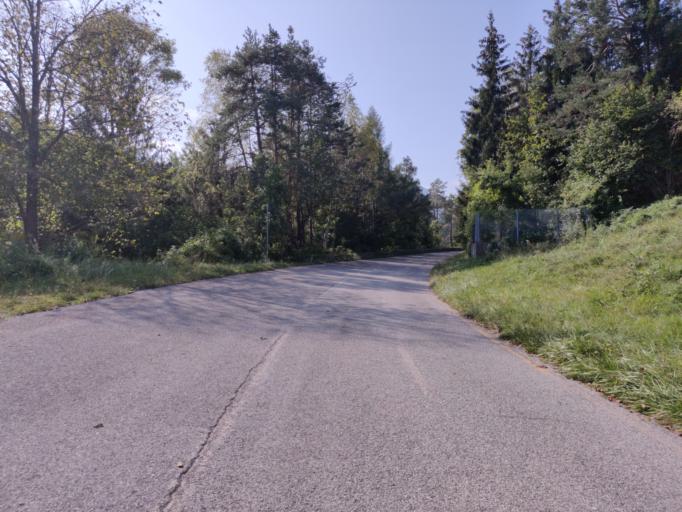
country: IT
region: Friuli Venezia Giulia
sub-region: Provincia di Udine
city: Tarvisio
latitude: 46.5156
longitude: 13.6151
